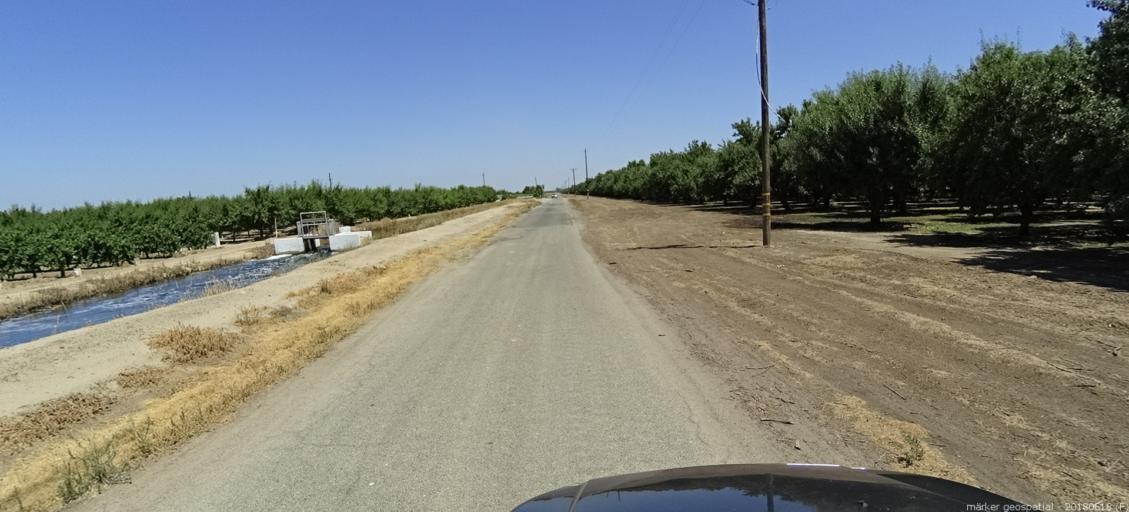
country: US
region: California
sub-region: Madera County
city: Parkwood
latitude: 36.8835
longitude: -120.1014
